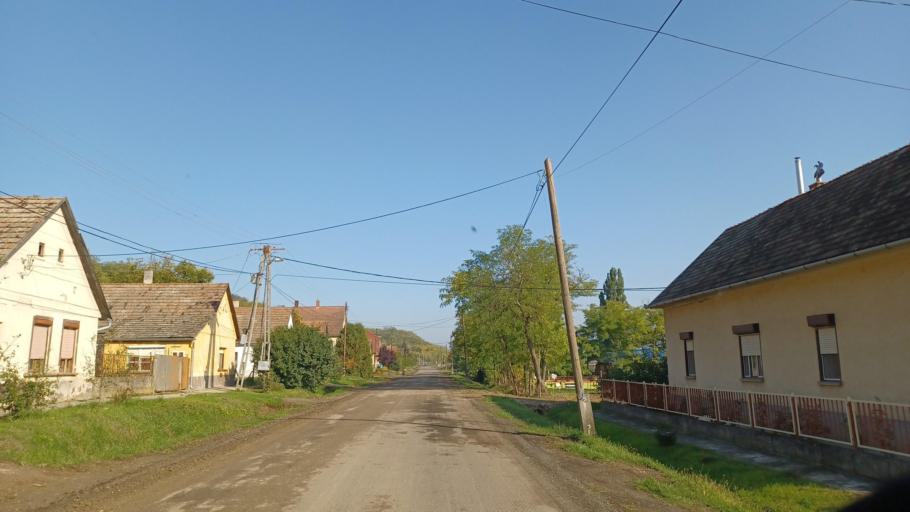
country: HU
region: Tolna
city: Szedres
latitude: 46.5143
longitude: 18.5904
